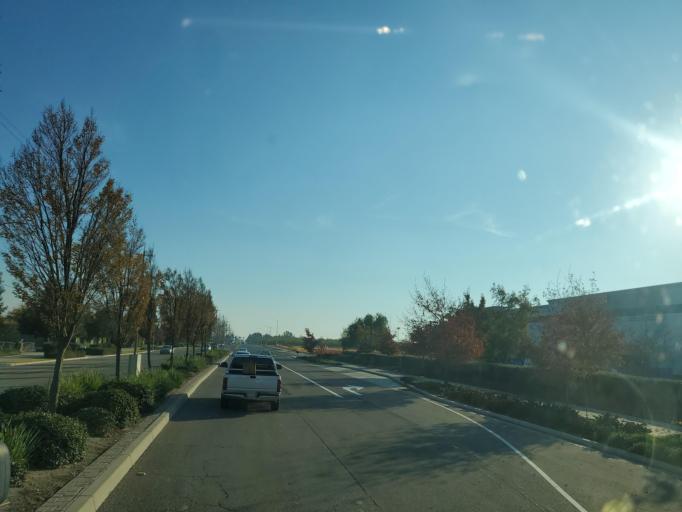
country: US
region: California
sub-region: San Joaquin County
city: Lathrop
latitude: 37.8318
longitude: -121.2542
